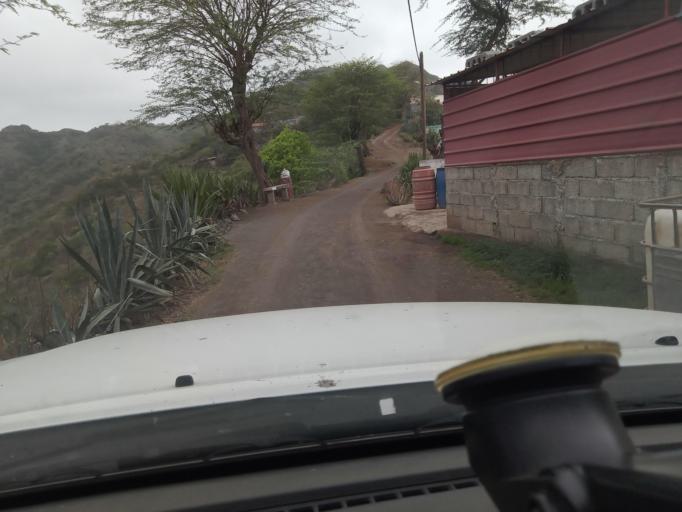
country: CV
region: Santa Catarina
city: Assomada
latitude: 15.1394
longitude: -23.6436
